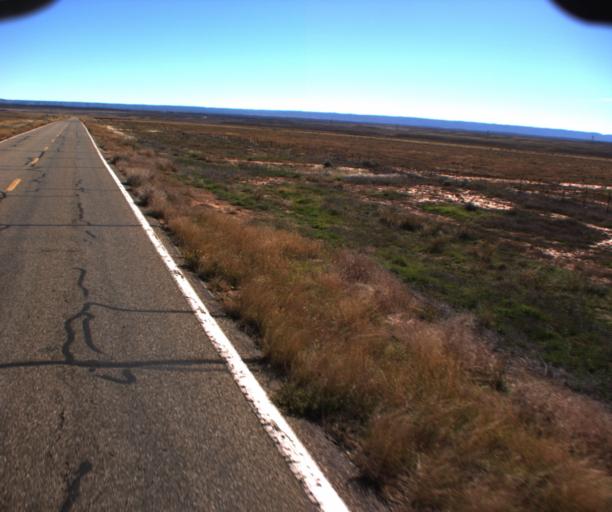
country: US
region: Arizona
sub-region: Coconino County
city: Fredonia
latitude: 36.9248
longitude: -112.4617
